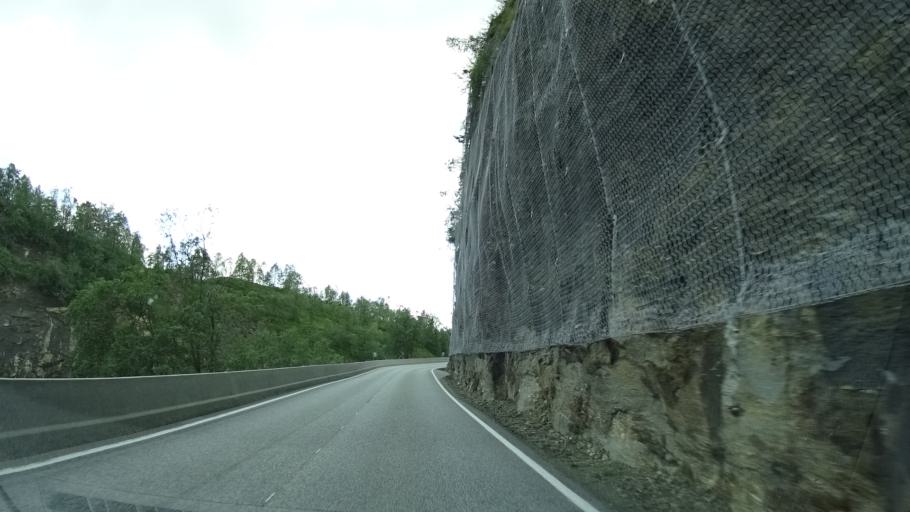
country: NO
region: Hordaland
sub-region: Kvam
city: Norheimsund
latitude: 60.3695
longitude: 6.0327
